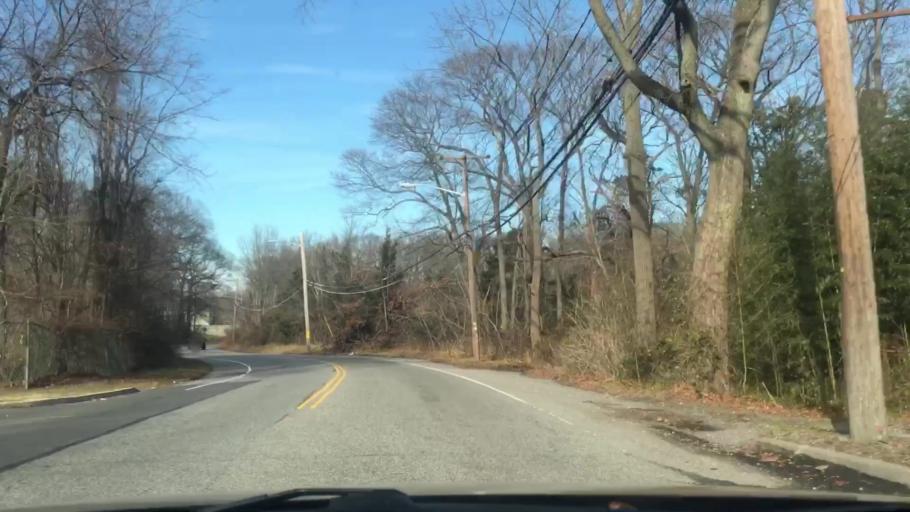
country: US
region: New York
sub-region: Suffolk County
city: Ronkonkoma
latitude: 40.8280
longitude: -73.1102
